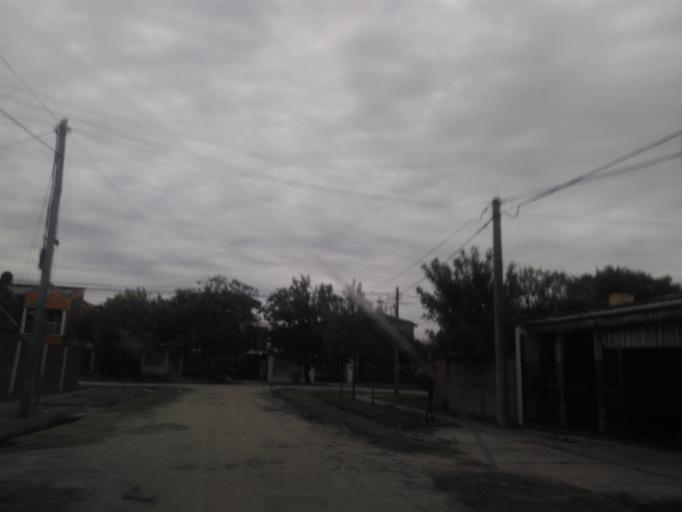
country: AR
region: Chaco
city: Resistencia
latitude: -27.4646
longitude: -59.0057
